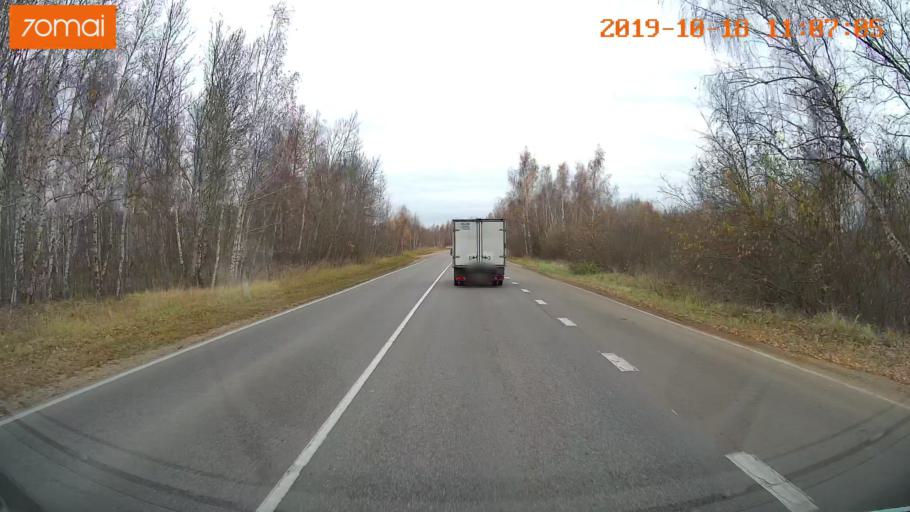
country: RU
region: Tula
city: Kimovsk
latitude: 53.9246
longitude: 38.5349
